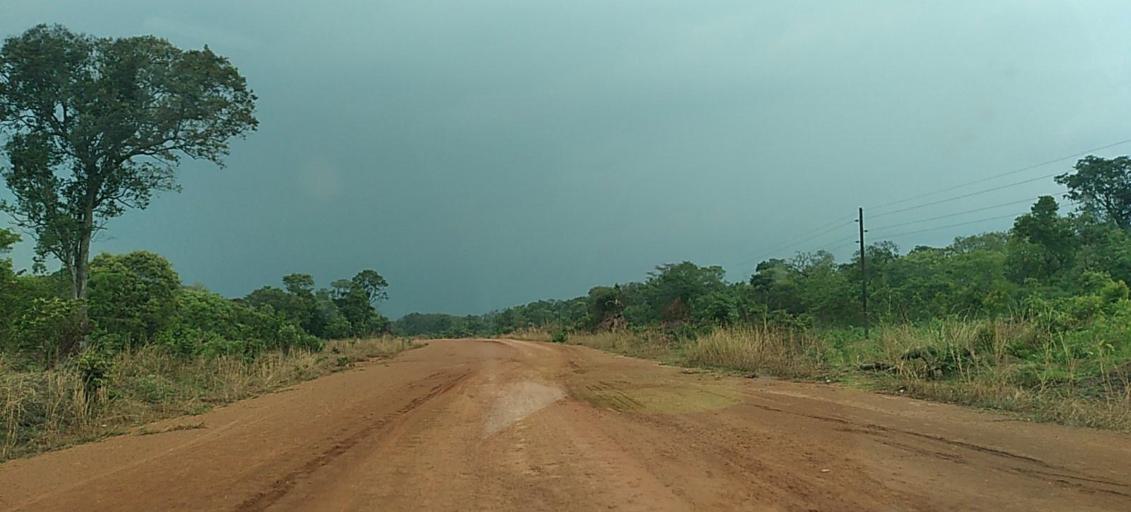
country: ZM
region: North-Western
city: Mwinilunga
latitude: -11.6394
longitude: 24.3997
